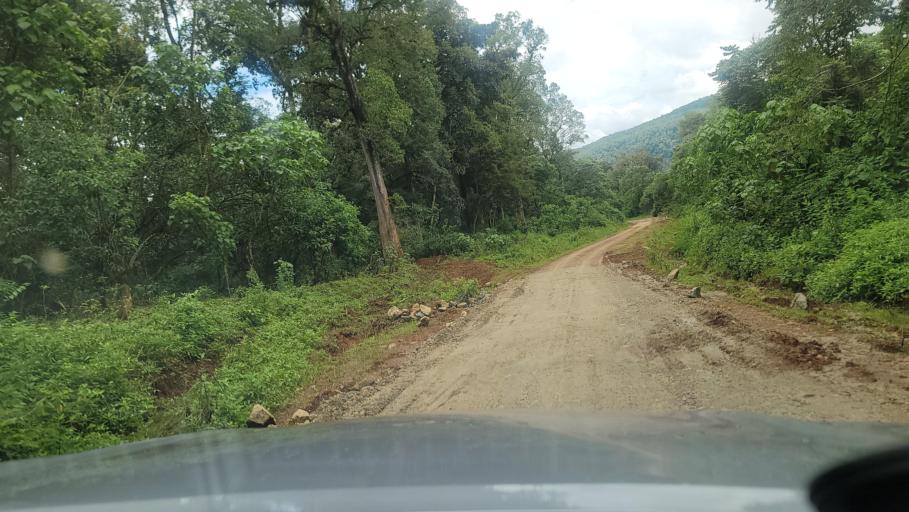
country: ET
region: Southern Nations, Nationalities, and People's Region
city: Bonga
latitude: 7.6209
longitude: 36.2093
